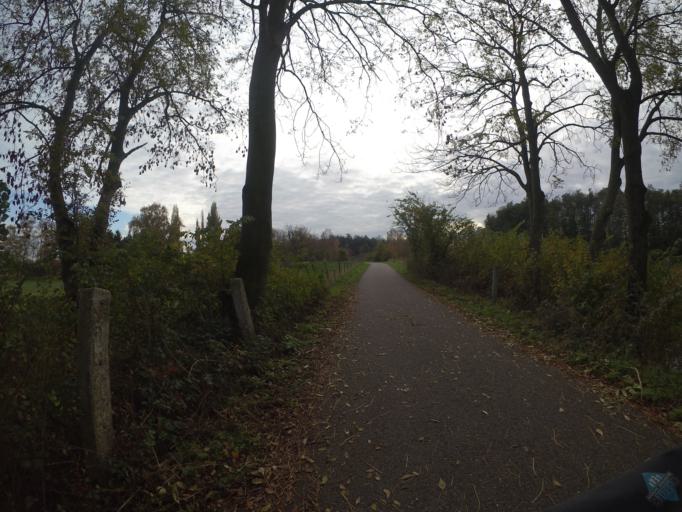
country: NL
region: North Brabant
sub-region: Gemeente Heusden
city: Heusden
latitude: 51.7086
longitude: 5.1104
